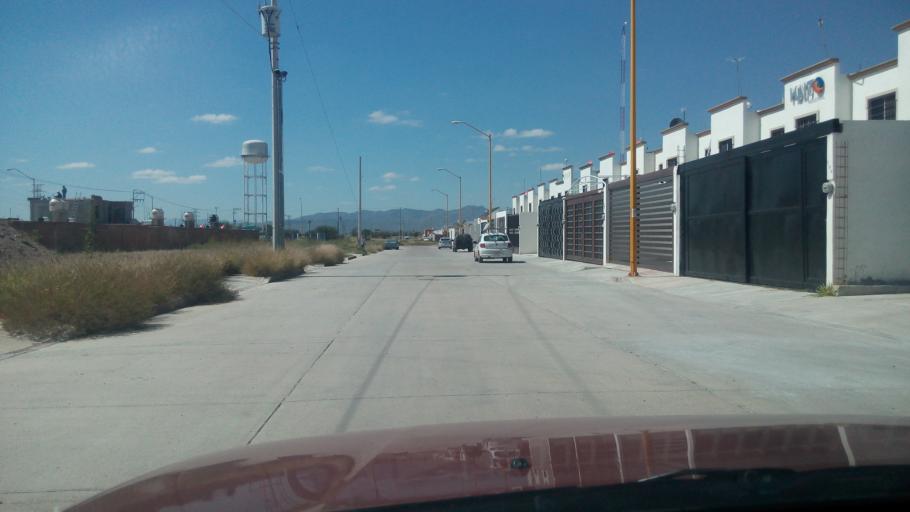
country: MX
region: Aguascalientes
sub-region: Aguascalientes
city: San Sebastian [Fraccionamiento]
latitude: 21.8368
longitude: -102.2952
